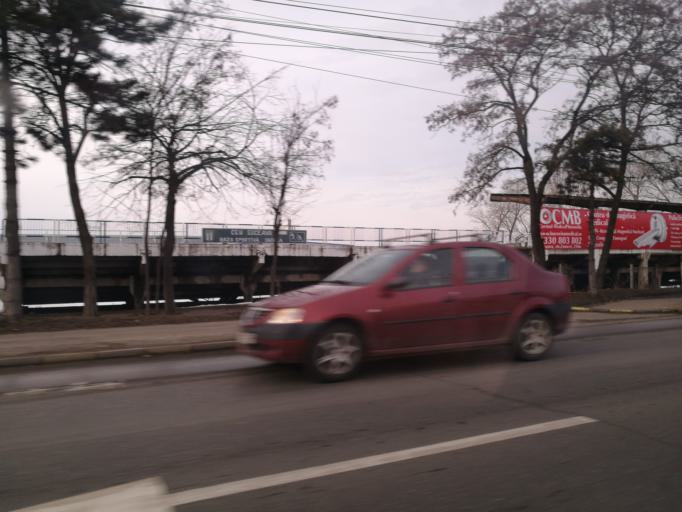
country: RO
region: Suceava
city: Suceava
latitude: 47.6566
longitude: 26.2623
